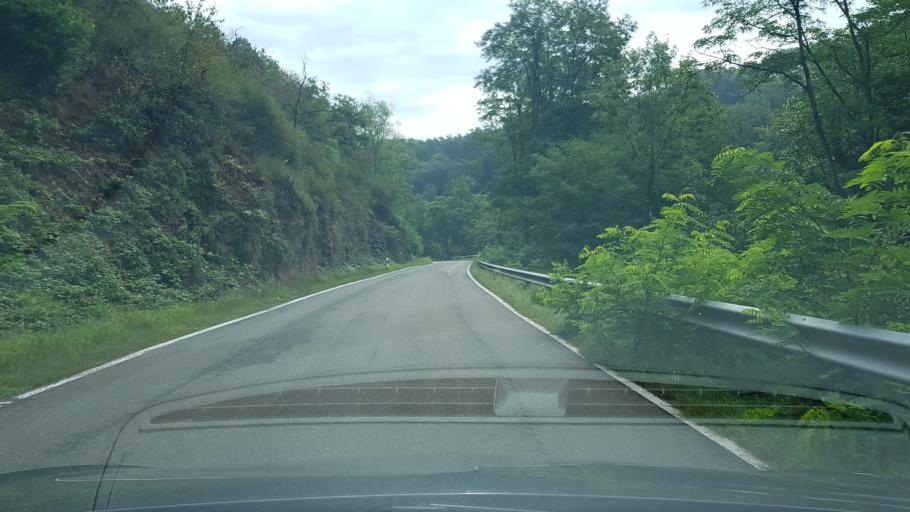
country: DE
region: Rheinland-Pfalz
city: Burgen
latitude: 50.2275
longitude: 7.3978
